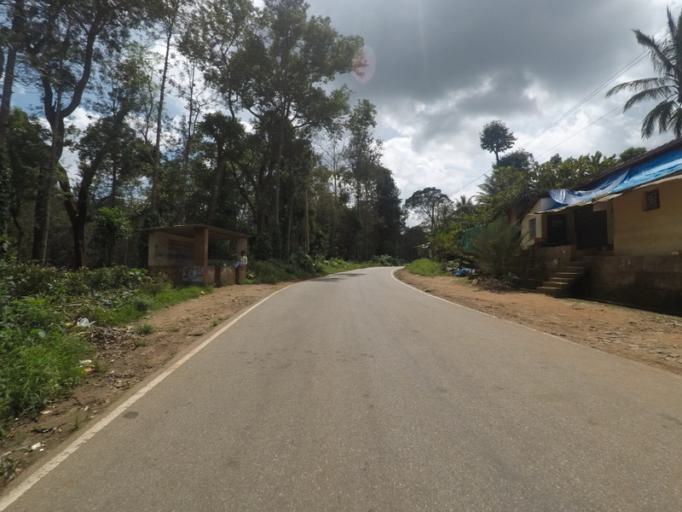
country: IN
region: Karnataka
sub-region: Kodagu
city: Suntikoppa
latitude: 12.3367
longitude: 75.8640
